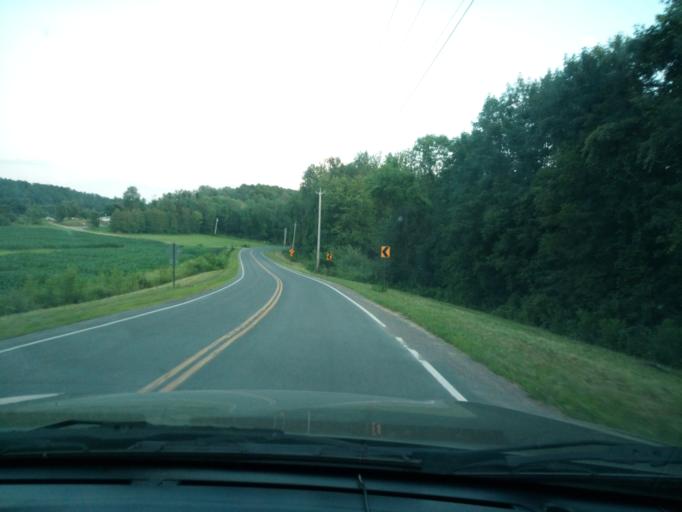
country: US
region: New York
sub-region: Wayne County
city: Clyde
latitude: 43.0658
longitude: -76.7753
